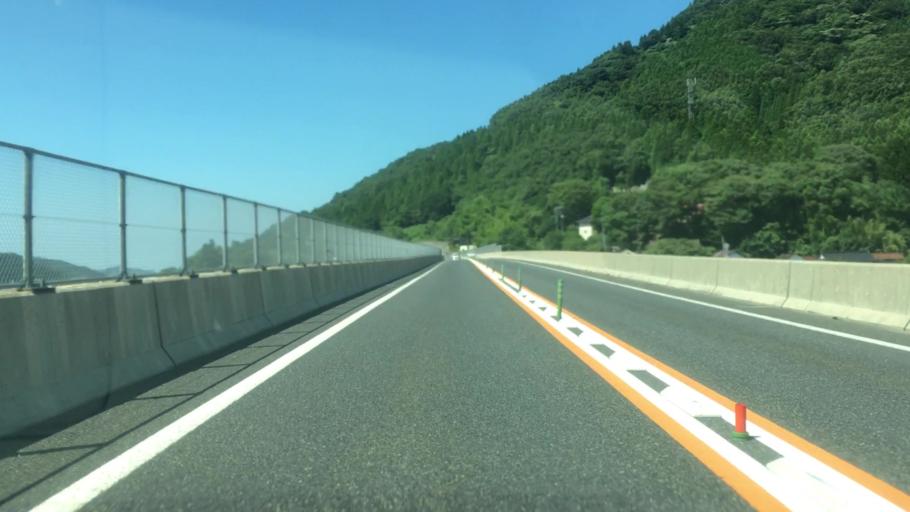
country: JP
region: Tottori
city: Tottori
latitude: 35.4060
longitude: 134.2061
